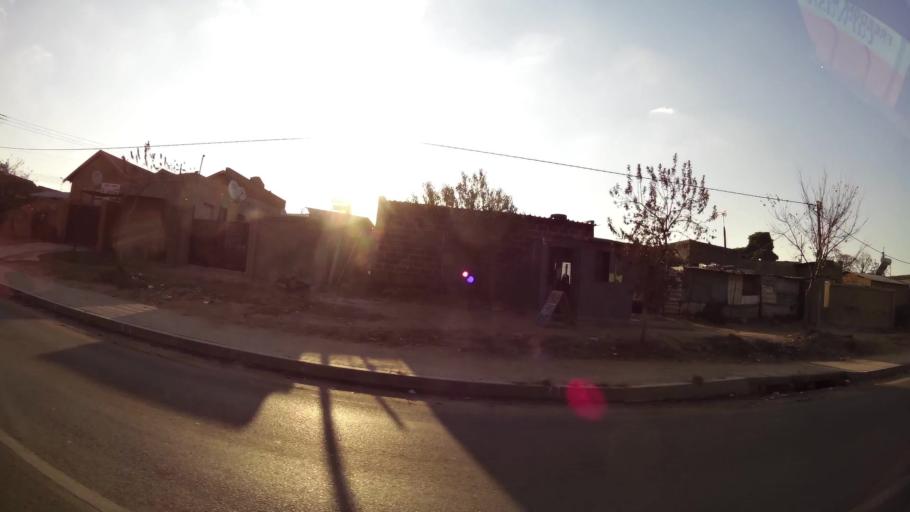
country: ZA
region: Gauteng
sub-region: Ekurhuleni Metropolitan Municipality
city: Tembisa
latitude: -26.0159
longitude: 28.1832
